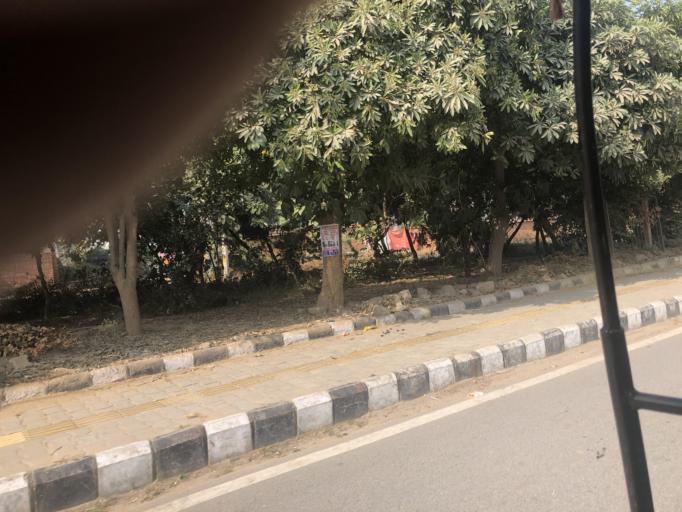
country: IN
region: Haryana
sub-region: Gurgaon
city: Gurgaon
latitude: 28.4267
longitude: 77.0911
